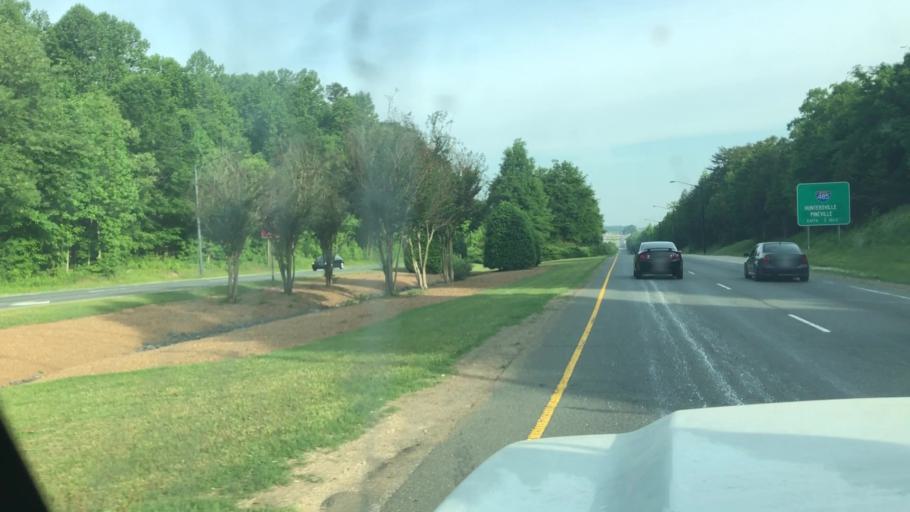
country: US
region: North Carolina
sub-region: Gaston County
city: Mount Holly
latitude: 35.3102
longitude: -80.9261
